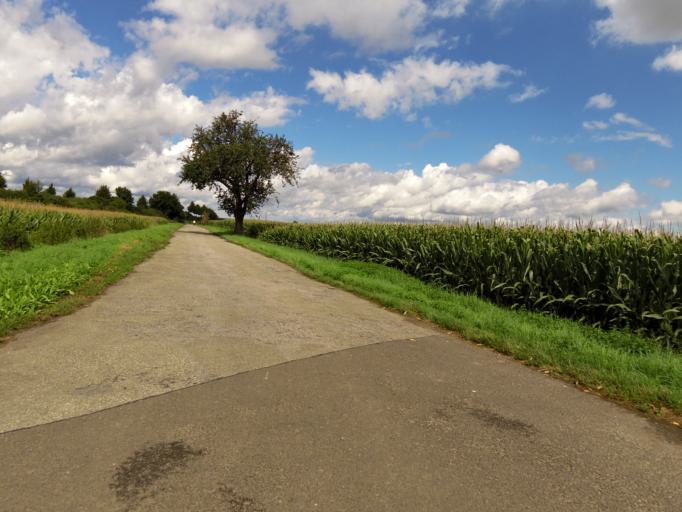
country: DE
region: Hesse
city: Lampertheim
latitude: 49.5649
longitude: 8.4483
